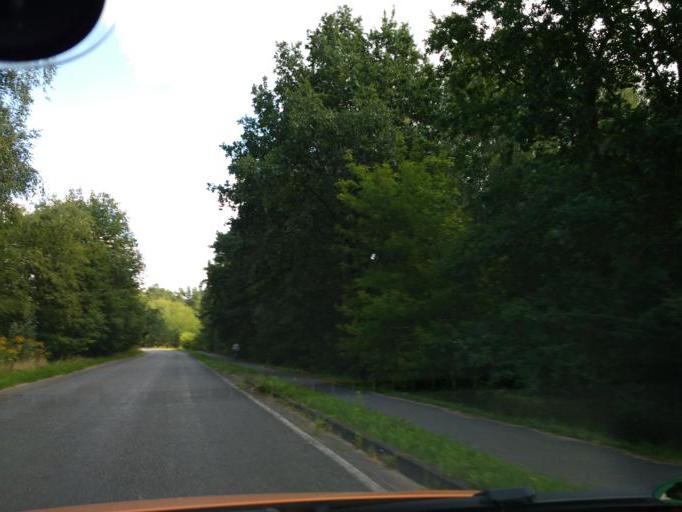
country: DE
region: Brandenburg
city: Wandlitz
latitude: 52.7473
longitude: 13.4376
